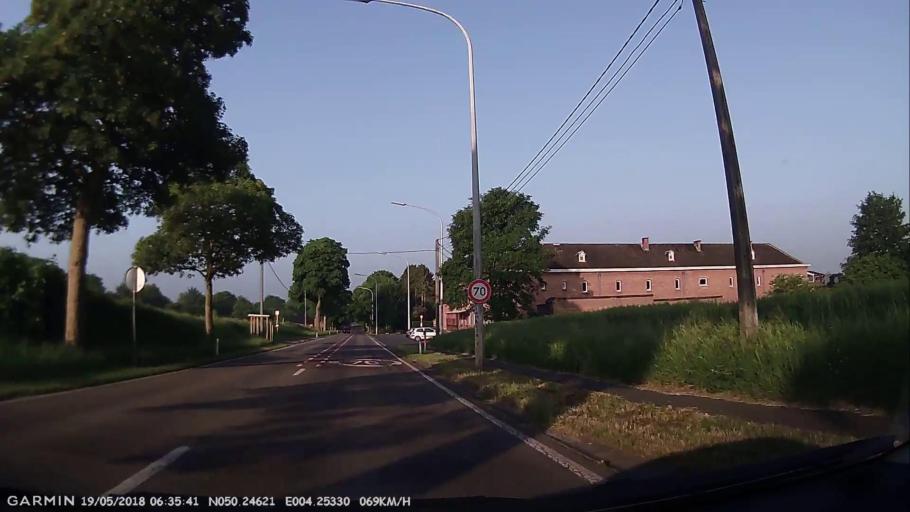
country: BE
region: Wallonia
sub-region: Province du Hainaut
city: Beaumont
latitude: 50.2462
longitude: 4.2532
